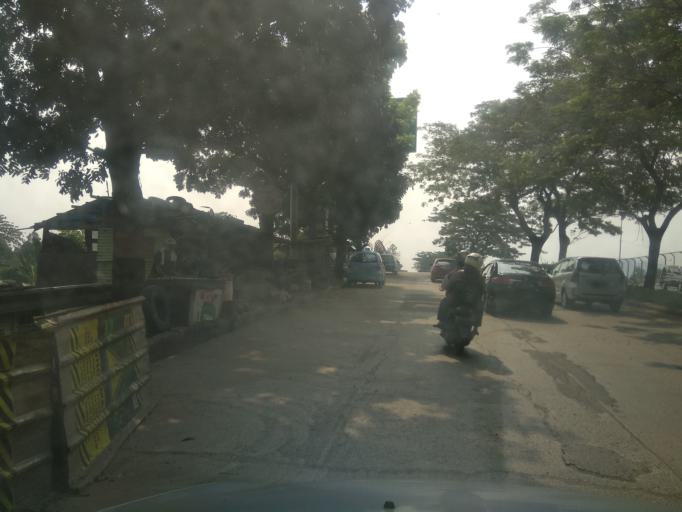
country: ID
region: West Java
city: Serpong
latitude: -6.3097
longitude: 106.6886
